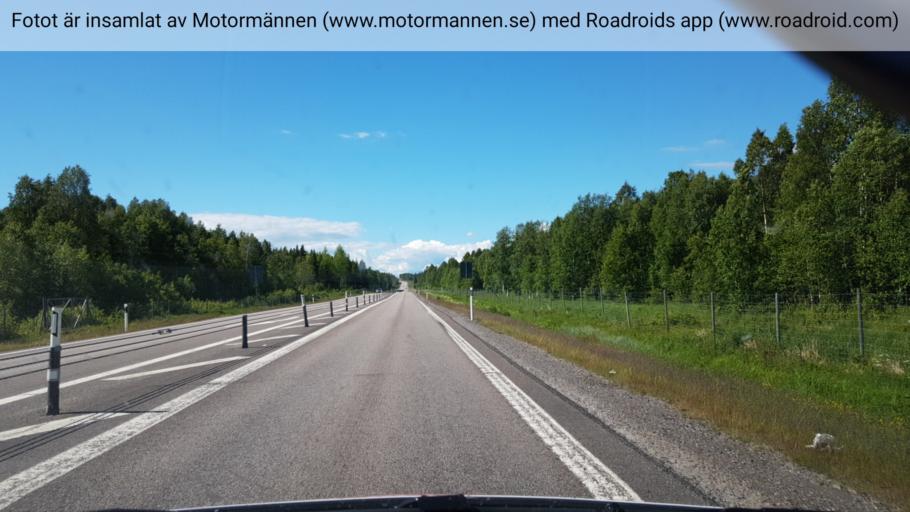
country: SE
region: Norrbotten
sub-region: Kalix Kommun
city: Rolfs
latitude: 65.8955
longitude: 22.8891
